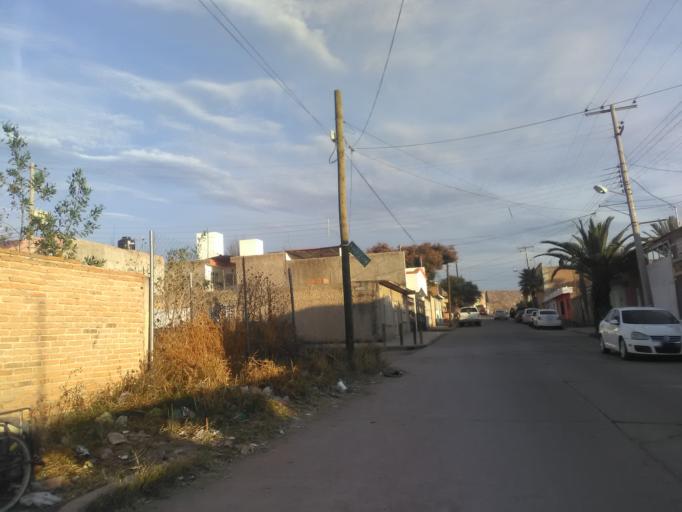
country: MX
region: Durango
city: Victoria de Durango
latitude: 24.0426
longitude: -104.6638
